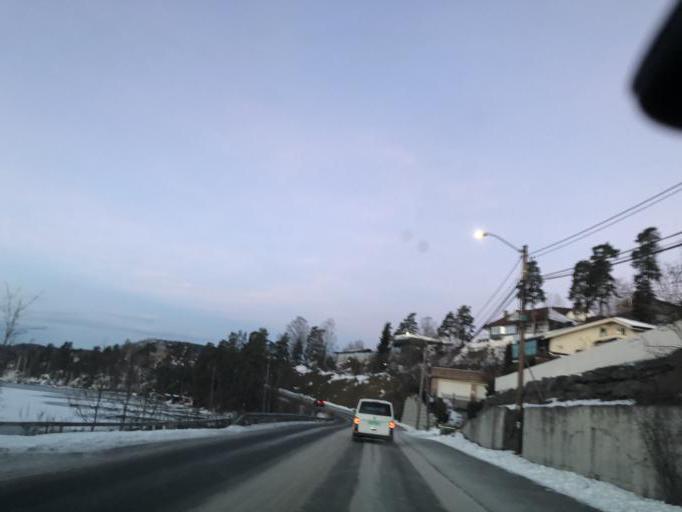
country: NO
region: Akershus
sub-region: Baerum
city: Sandvika
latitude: 59.8728
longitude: 10.5143
